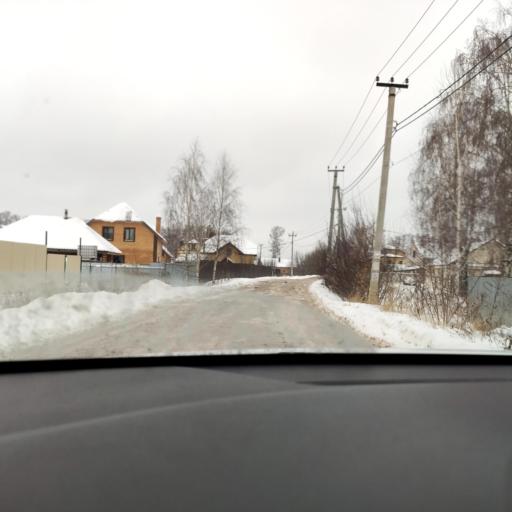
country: RU
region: Tatarstan
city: Vysokaya Gora
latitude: 55.8349
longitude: 49.2383
